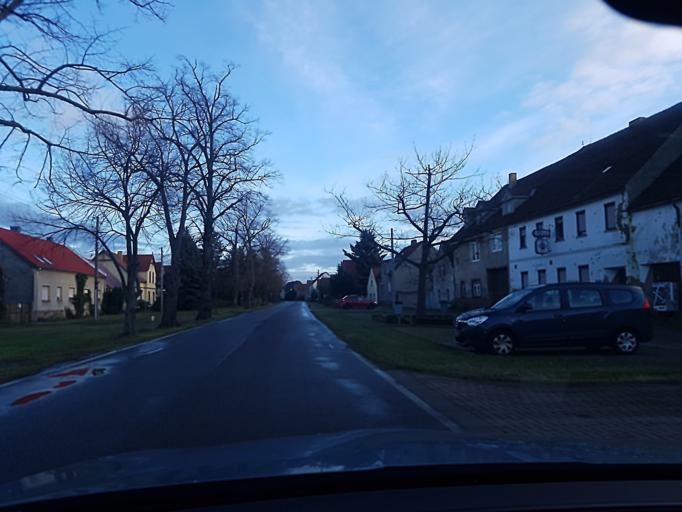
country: DE
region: Brandenburg
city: Trobitz
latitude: 51.5751
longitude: 13.4086
